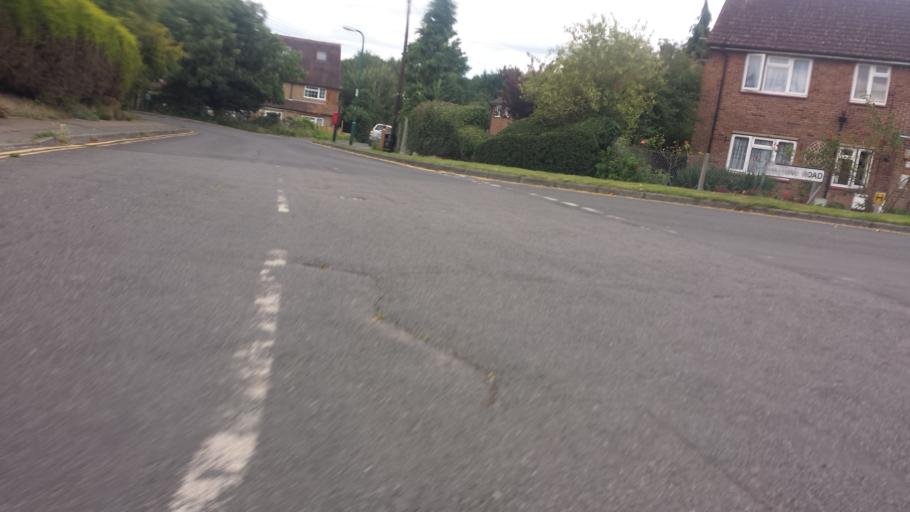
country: GB
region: England
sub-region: Kent
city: Swanley
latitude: 51.3801
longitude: 0.1605
